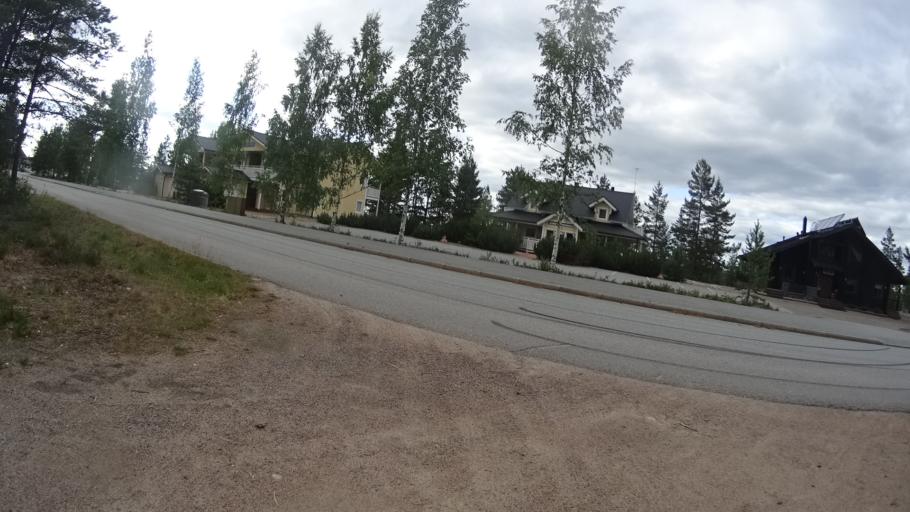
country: FI
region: Satakunta
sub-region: Pohjois-Satakunta
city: Jaemijaervi
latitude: 61.7782
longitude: 22.7204
